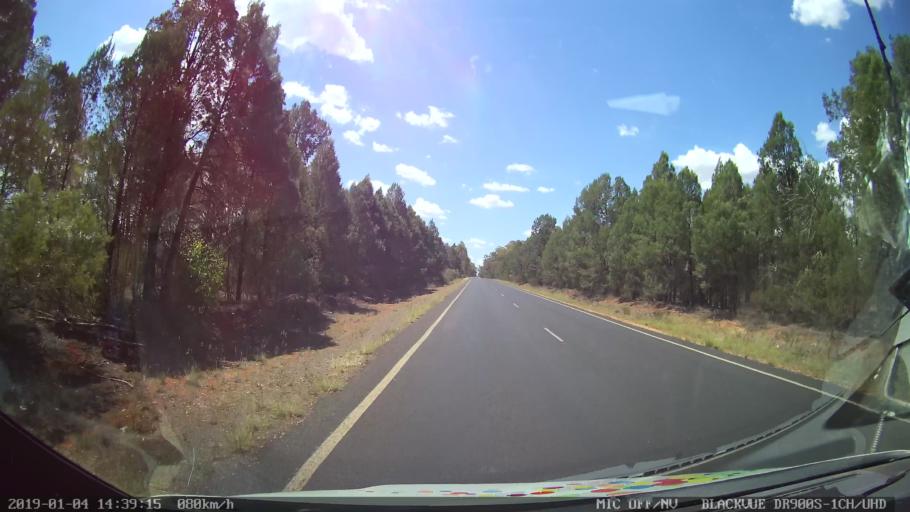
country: AU
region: New South Wales
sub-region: Dubbo Municipality
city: Dubbo
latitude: -32.1670
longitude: 148.6326
